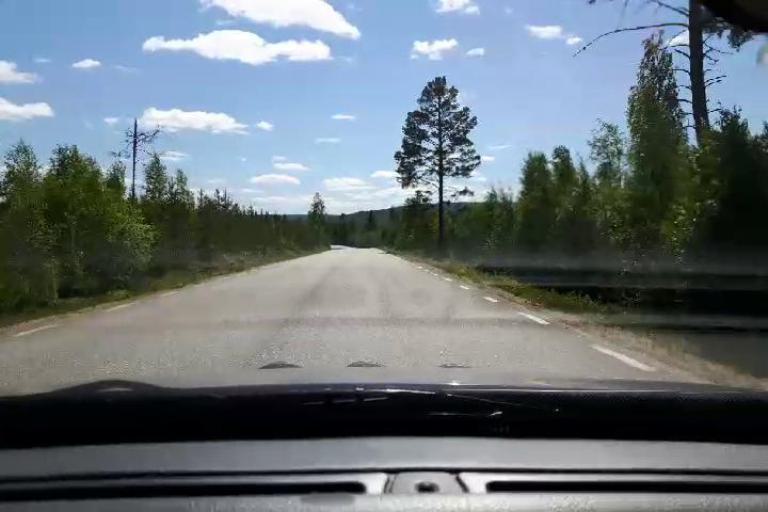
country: SE
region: Gaevleborg
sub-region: Ljusdals Kommun
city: Farila
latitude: 62.0037
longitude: 15.2400
